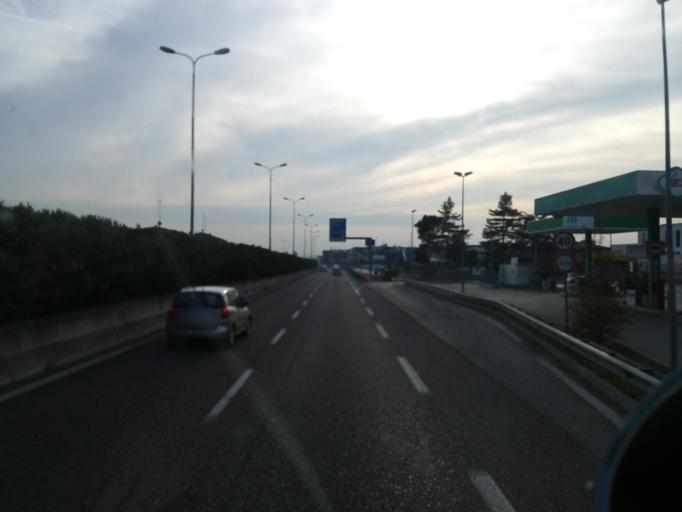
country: IT
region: Lombardy
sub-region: Provincia di Brescia
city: Desenzano del Garda
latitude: 45.4420
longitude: 10.5185
